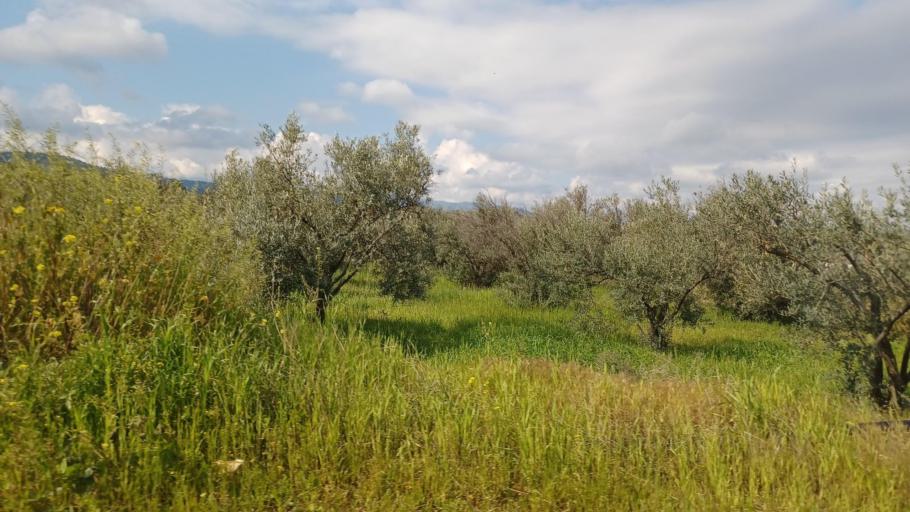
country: CY
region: Lefkosia
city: Astromeritis
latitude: 35.0823
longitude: 32.9562
